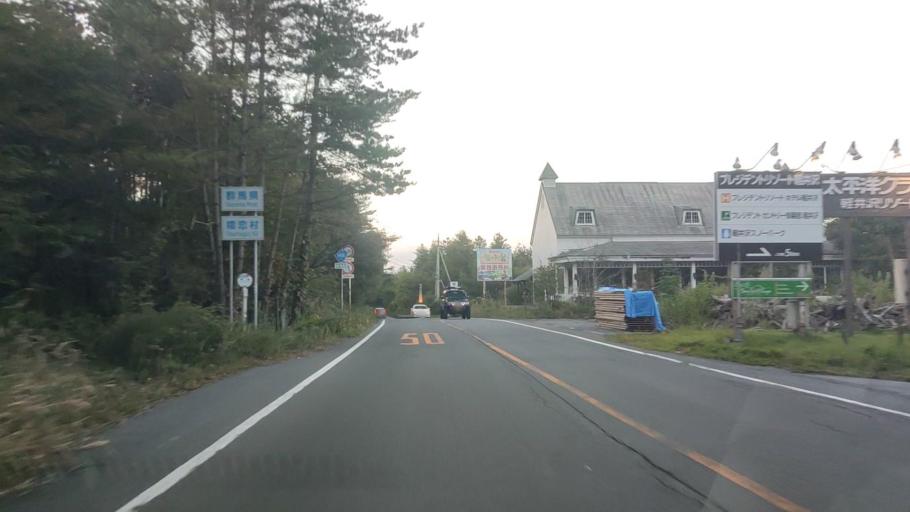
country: JP
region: Nagano
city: Komoro
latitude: 36.4196
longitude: 138.5707
